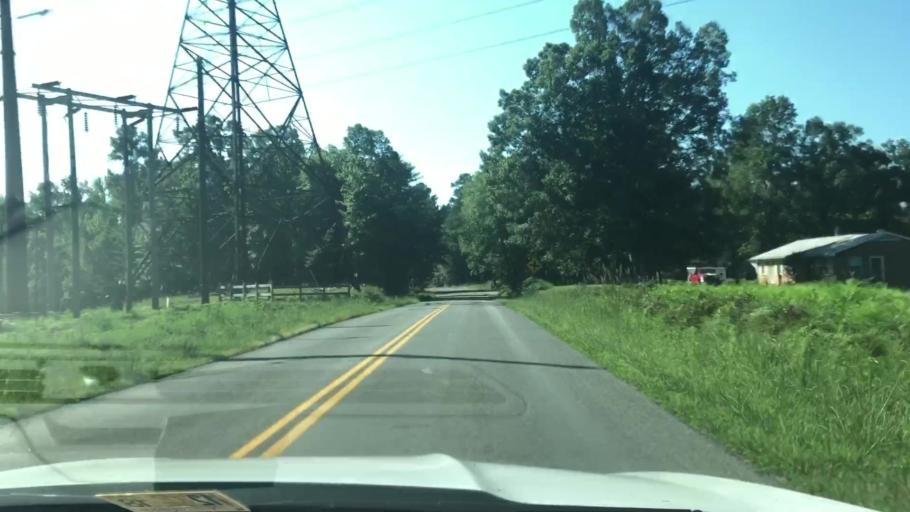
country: US
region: Virginia
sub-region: New Kent County
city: New Kent
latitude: 37.4205
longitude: -76.9129
